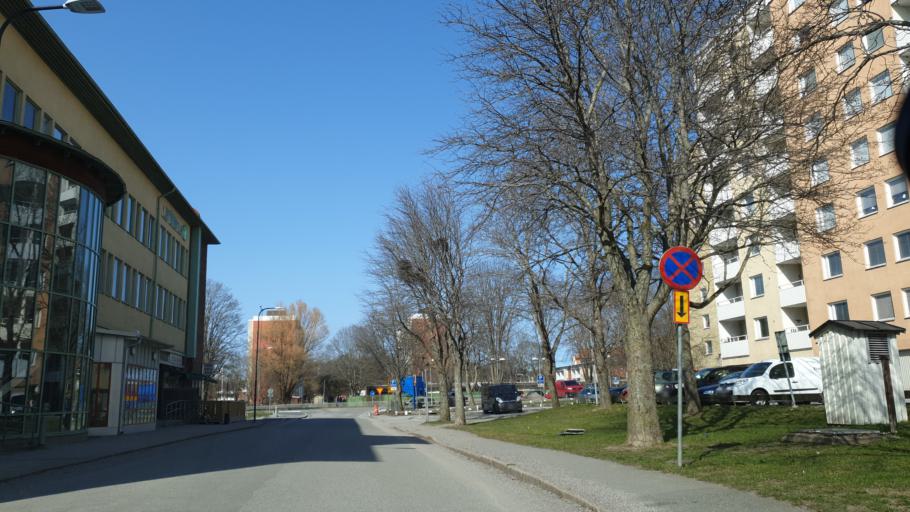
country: SE
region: Stockholm
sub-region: Jarfalla Kommun
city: Jakobsberg
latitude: 59.4244
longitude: 17.8388
